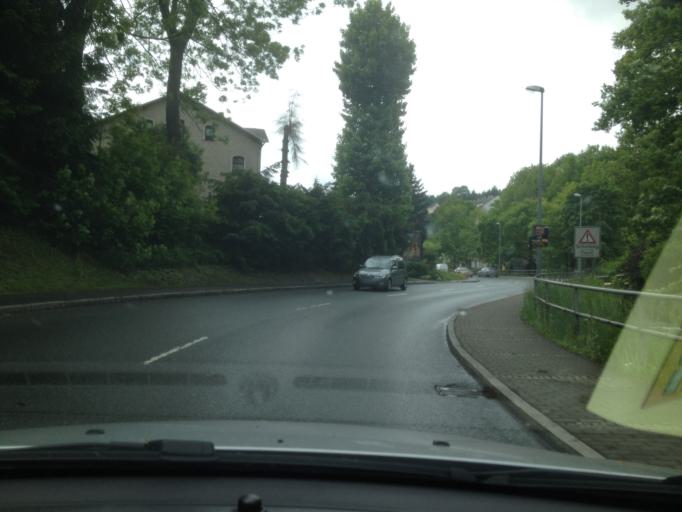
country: DE
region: Saxony
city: Annaberg-Buchholz
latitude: 50.5683
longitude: 12.9989
